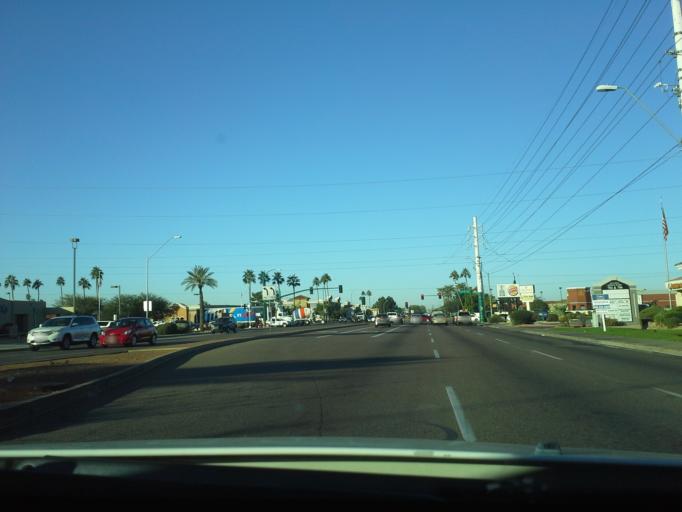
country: US
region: Arizona
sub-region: Maricopa County
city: Glendale
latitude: 33.6403
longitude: -112.0641
